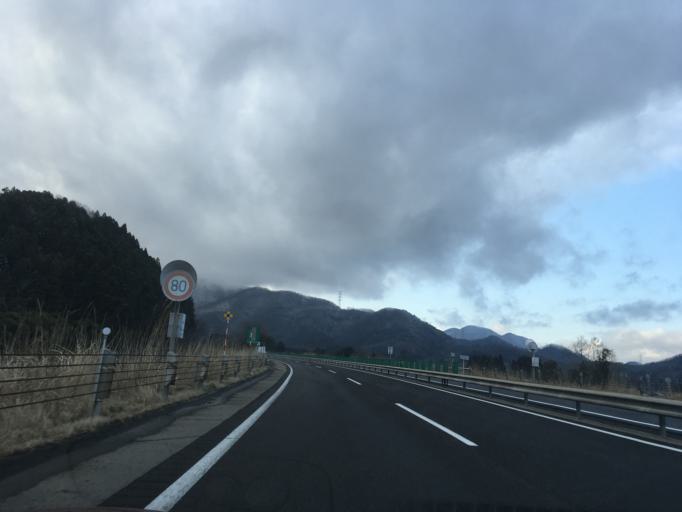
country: JP
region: Miyagi
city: Shiroishi
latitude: 38.1915
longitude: 140.5965
